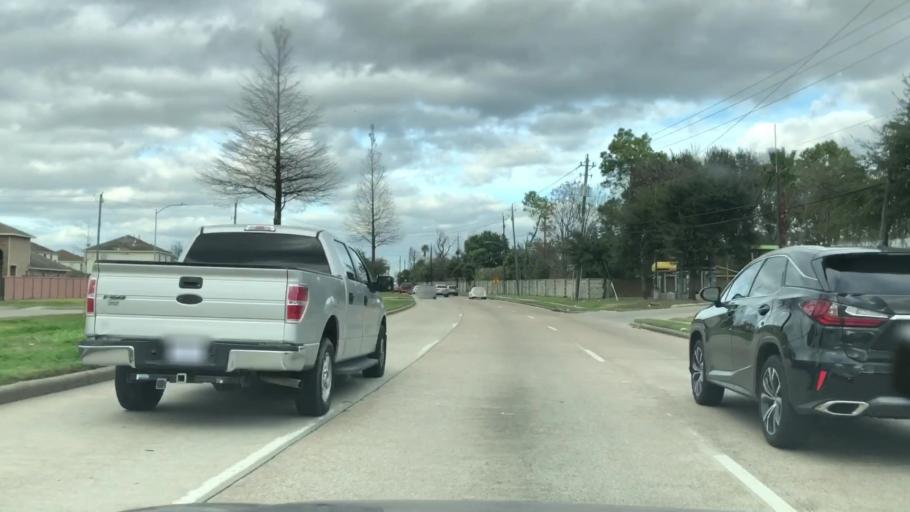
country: US
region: Texas
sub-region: Harris County
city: Bellaire
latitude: 29.6316
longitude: -95.4635
